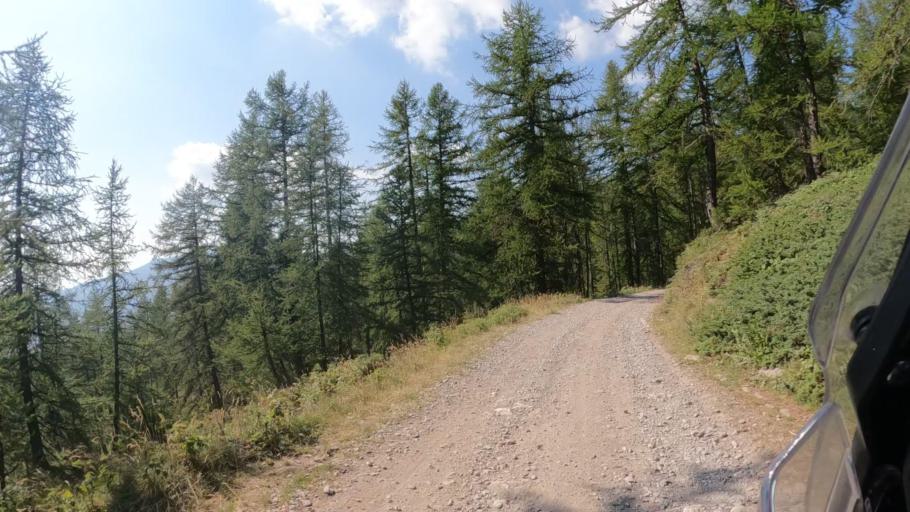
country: IT
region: Piedmont
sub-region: Provincia di Cuneo
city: Briga Alta
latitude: 44.1015
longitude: 7.7188
